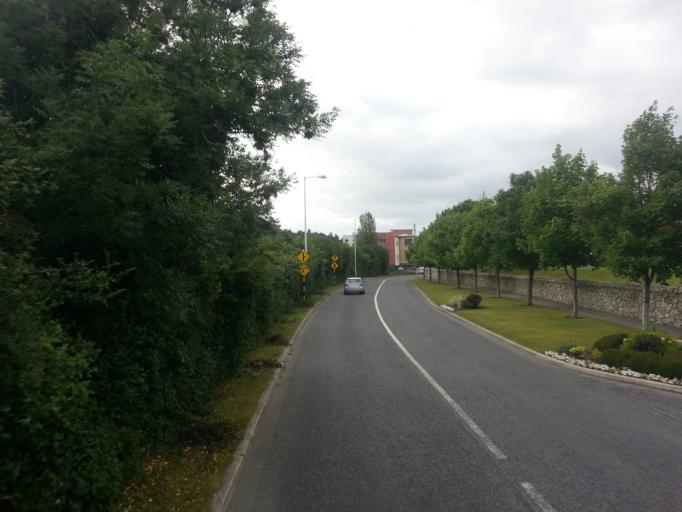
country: IE
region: Leinster
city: Sandyford
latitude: 53.2512
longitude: -6.2114
